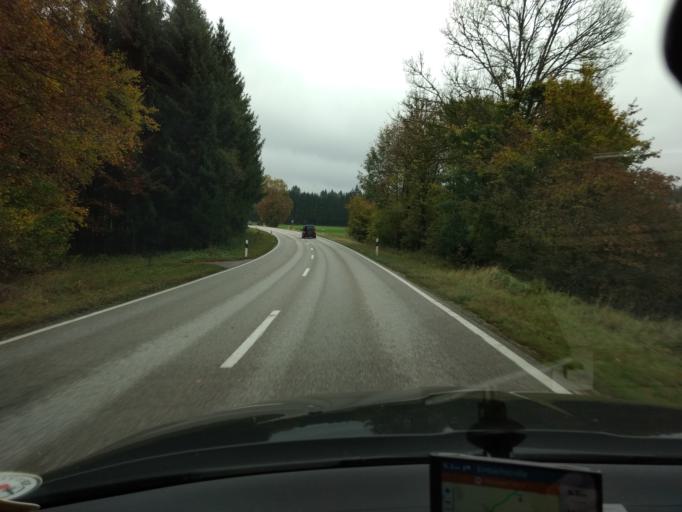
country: DE
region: Bavaria
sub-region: Upper Bavaria
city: Konigsdorf
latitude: 47.8130
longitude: 11.5052
